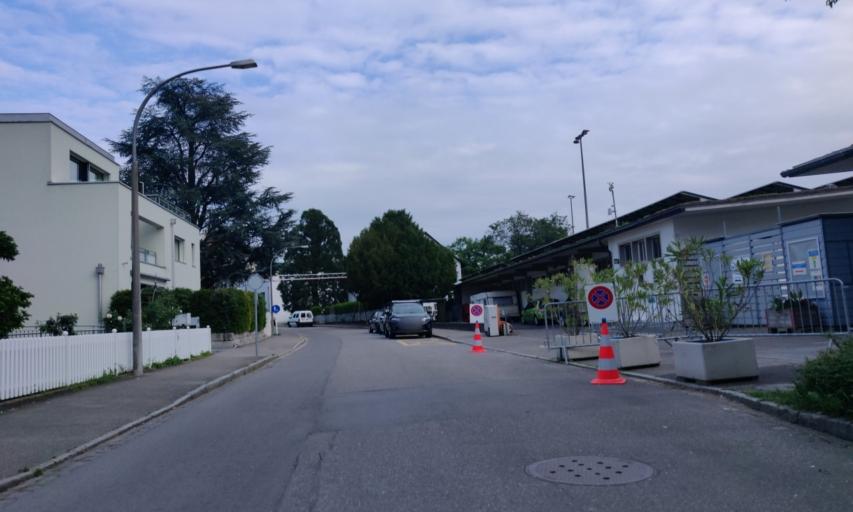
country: CH
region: Basel-City
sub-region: Basel-Stadt
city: Riehen
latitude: 47.5812
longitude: 7.6391
